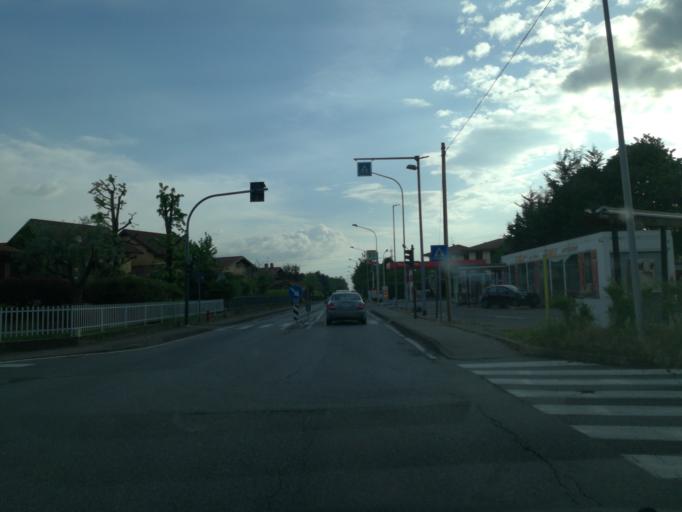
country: IT
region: Lombardy
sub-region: Provincia di Lecco
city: Paderno d'Adda
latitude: 45.6759
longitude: 9.4468
